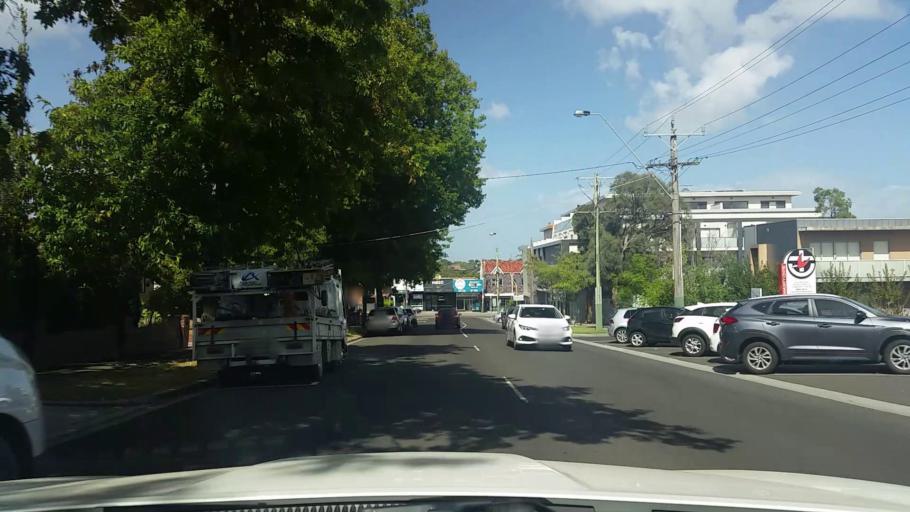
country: AU
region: Victoria
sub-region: Stonnington
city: Glen Iris
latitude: -37.8607
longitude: 145.0661
